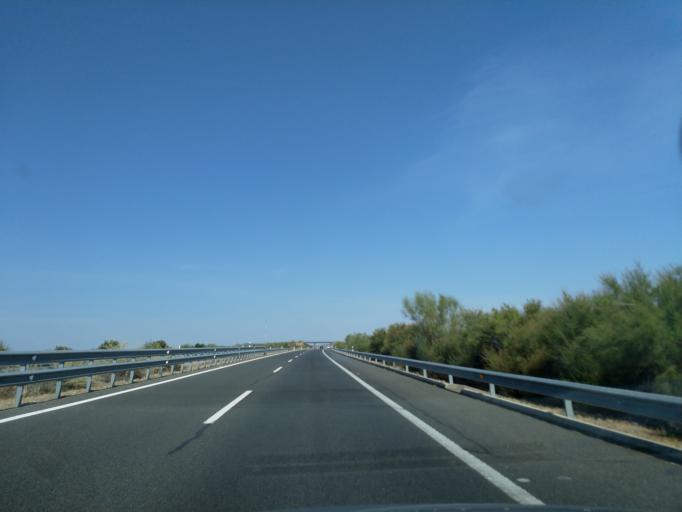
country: ES
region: Extremadura
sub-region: Provincia de Caceres
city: Aldea del Cano
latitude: 39.3223
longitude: -6.3298
